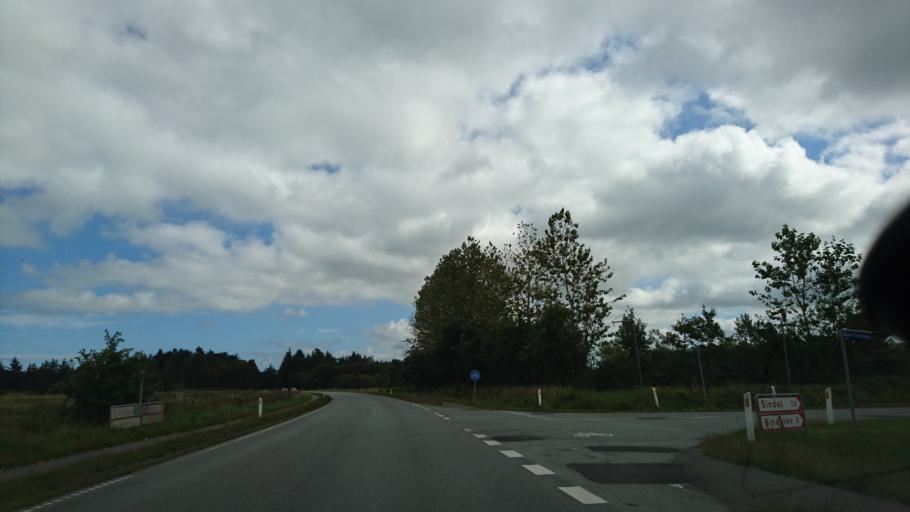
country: DK
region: North Denmark
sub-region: Hjorring Kommune
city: Sindal
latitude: 57.5807
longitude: 10.2103
